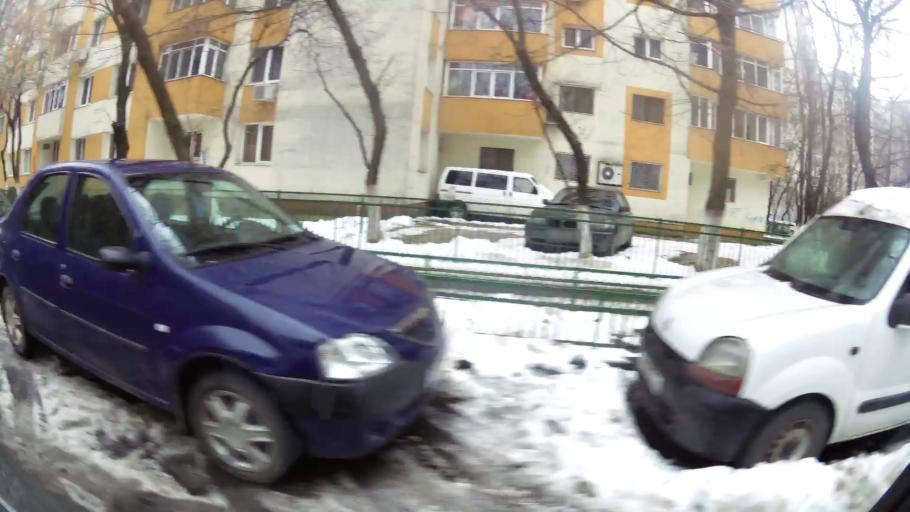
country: RO
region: Bucuresti
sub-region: Municipiul Bucuresti
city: Bucuresti
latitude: 44.4119
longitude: 26.0622
